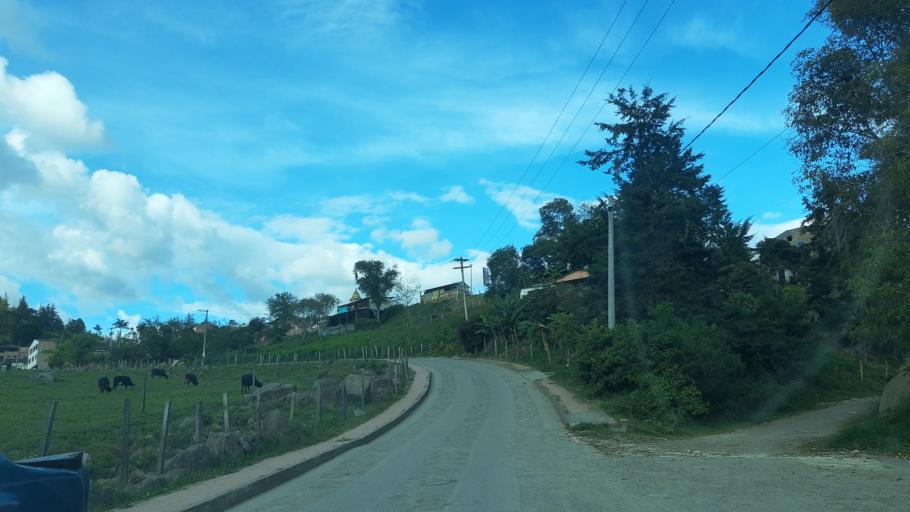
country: CO
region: Cundinamarca
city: Macheta
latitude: 5.0788
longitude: -73.6101
